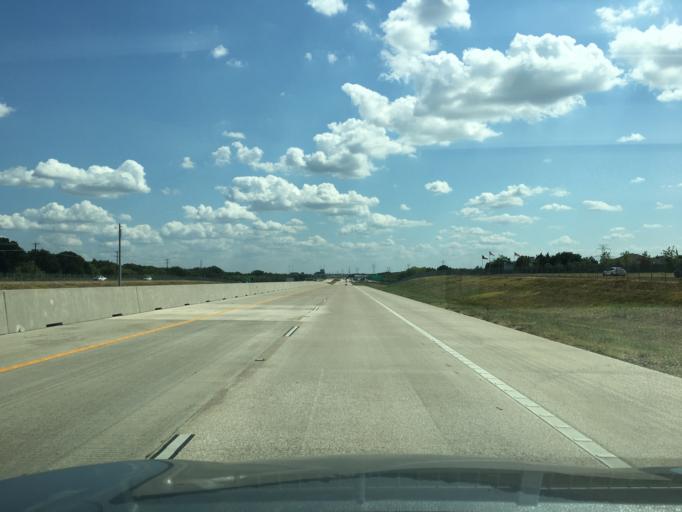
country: US
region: Texas
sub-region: Tarrant County
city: Mansfield
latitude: 32.6010
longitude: -97.0775
